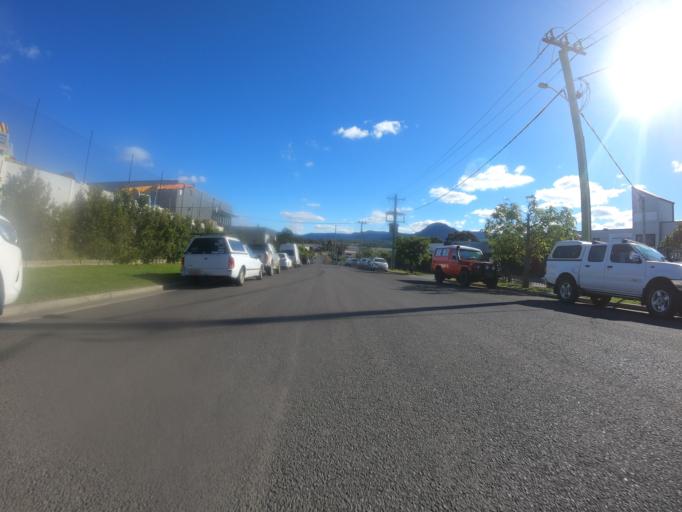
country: AU
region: New South Wales
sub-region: Wollongong
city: Berkeley
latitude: -34.4645
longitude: 150.8591
